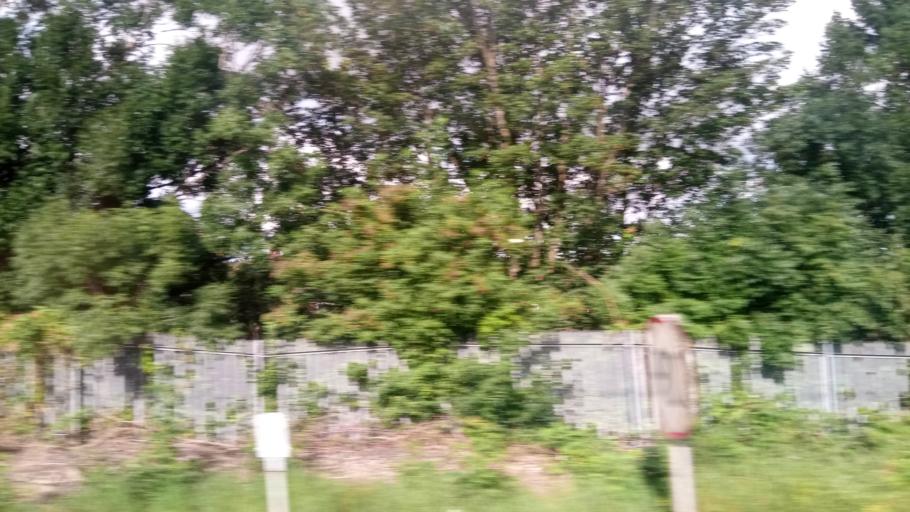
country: GB
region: England
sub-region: Darlington
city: Darlington
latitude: 54.5138
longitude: -1.5476
